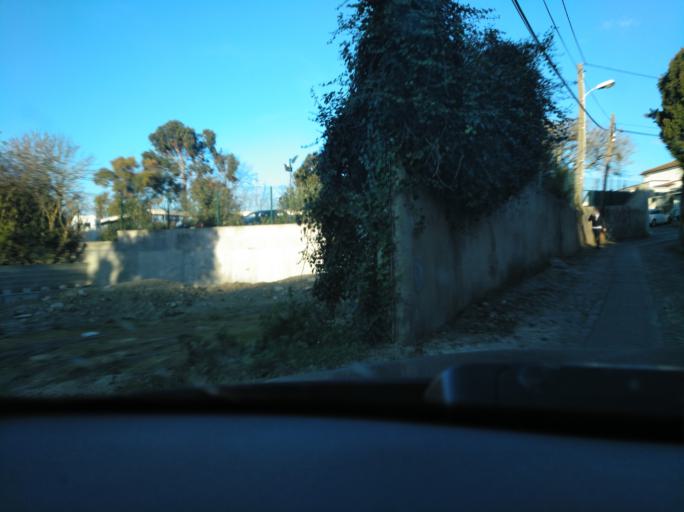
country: PT
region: Lisbon
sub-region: Odivelas
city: Olival do Basto
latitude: 38.7734
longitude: -9.1749
